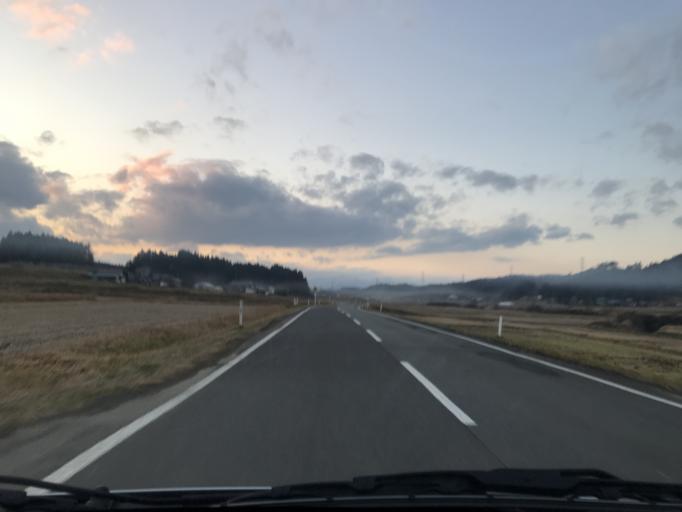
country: JP
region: Iwate
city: Ichinoseki
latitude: 38.8422
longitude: 141.1219
